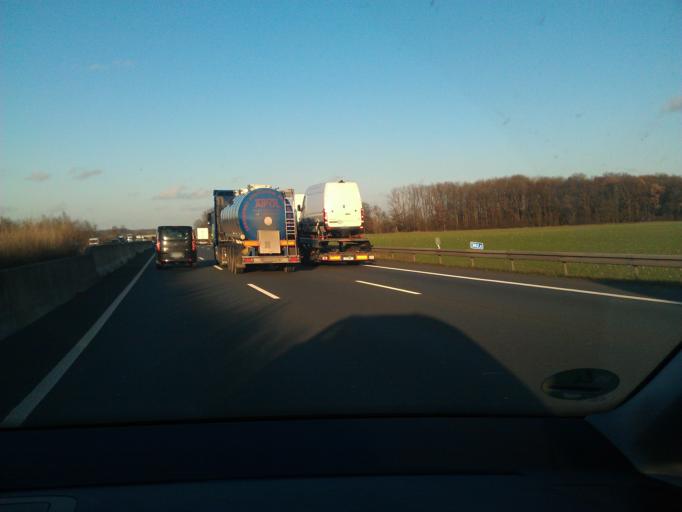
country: DE
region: North Rhine-Westphalia
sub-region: Regierungsbezirk Munster
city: Beckum
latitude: 51.7383
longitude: 7.9887
